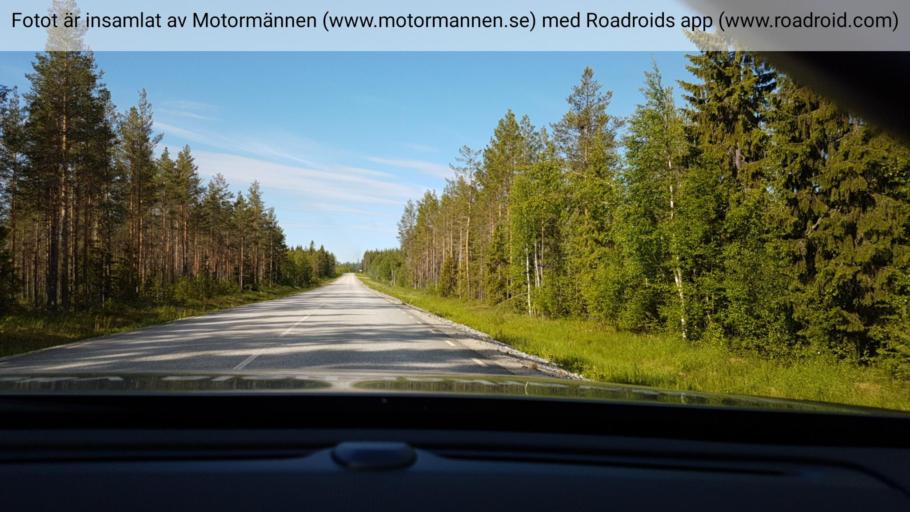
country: SE
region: Vaesterbotten
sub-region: Bjurholms Kommun
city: Bjurholm
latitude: 64.1585
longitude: 19.3644
